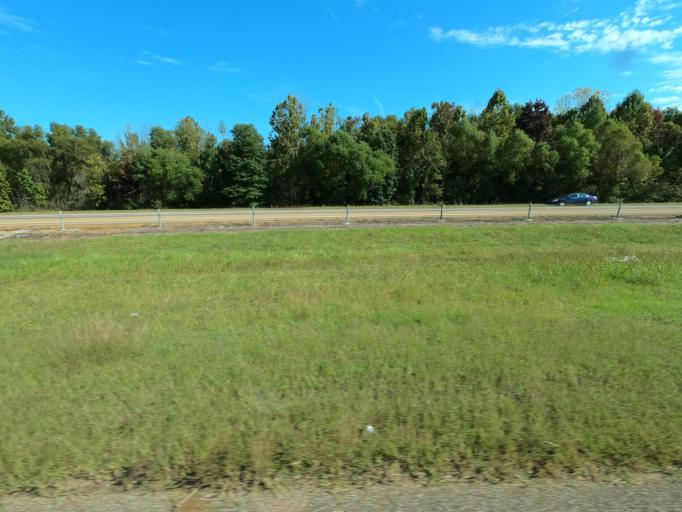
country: US
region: Tennessee
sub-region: Shelby County
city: Millington
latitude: 35.3156
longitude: -89.8676
